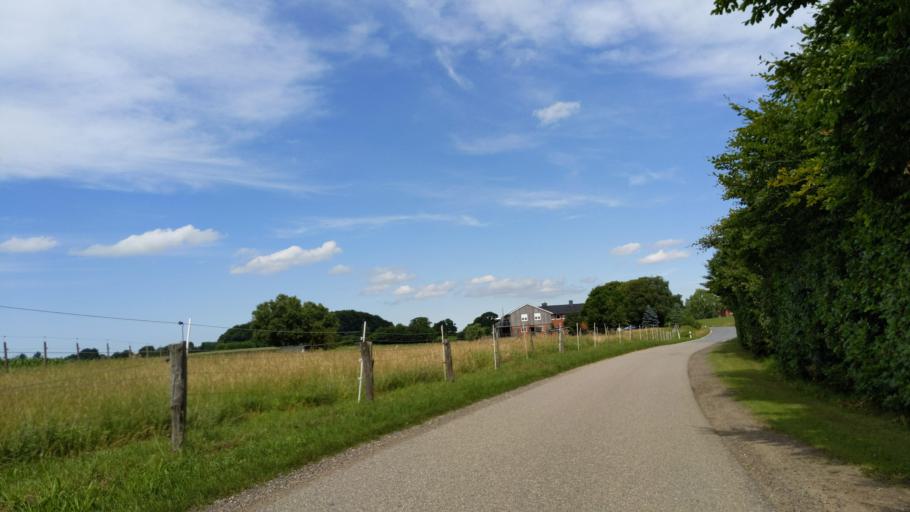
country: DE
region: Schleswig-Holstein
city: Kasseedorf
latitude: 54.1184
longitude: 10.7054
